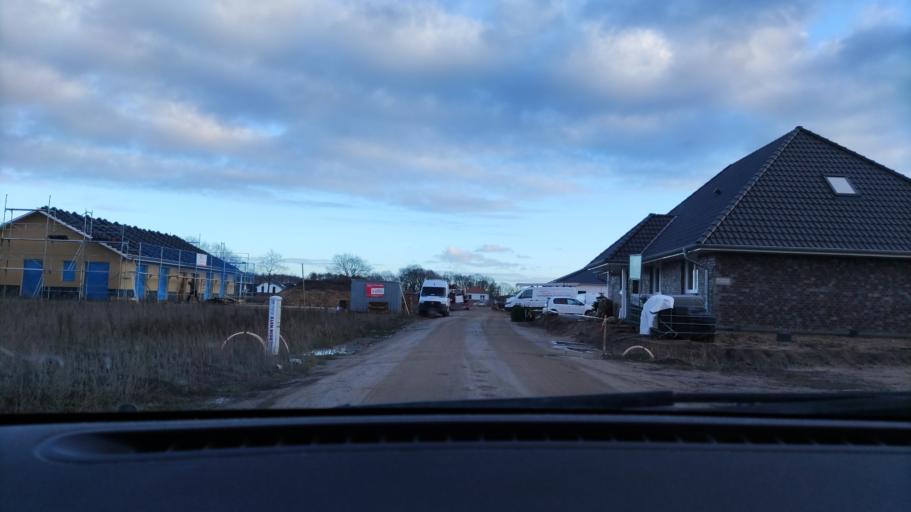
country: DE
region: Lower Saxony
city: Bienenbuttel
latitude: 53.1288
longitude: 10.4731
